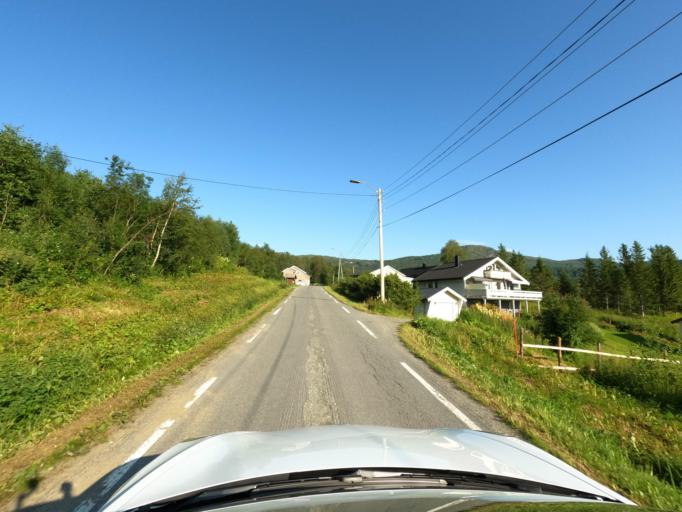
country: NO
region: Troms
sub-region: Gratangen
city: Gratangen
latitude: 68.5586
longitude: 17.7196
